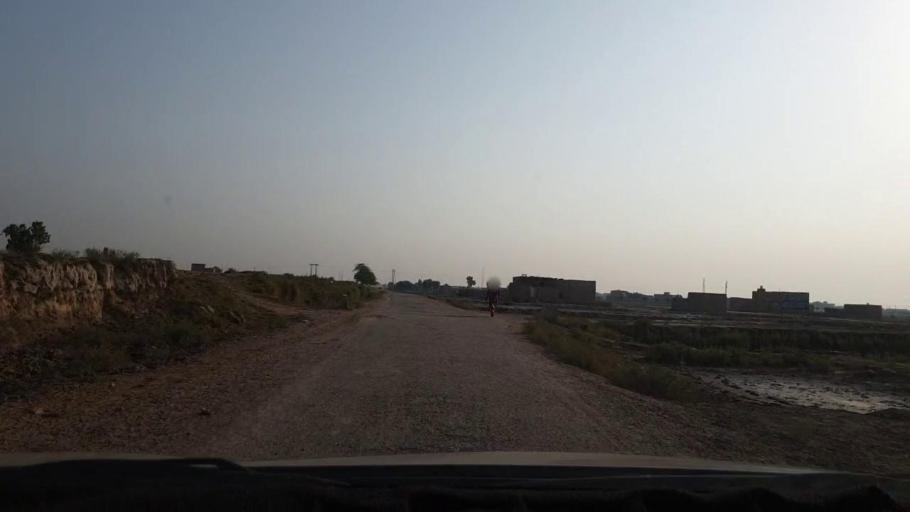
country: PK
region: Sindh
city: Larkana
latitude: 27.5255
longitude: 68.1957
